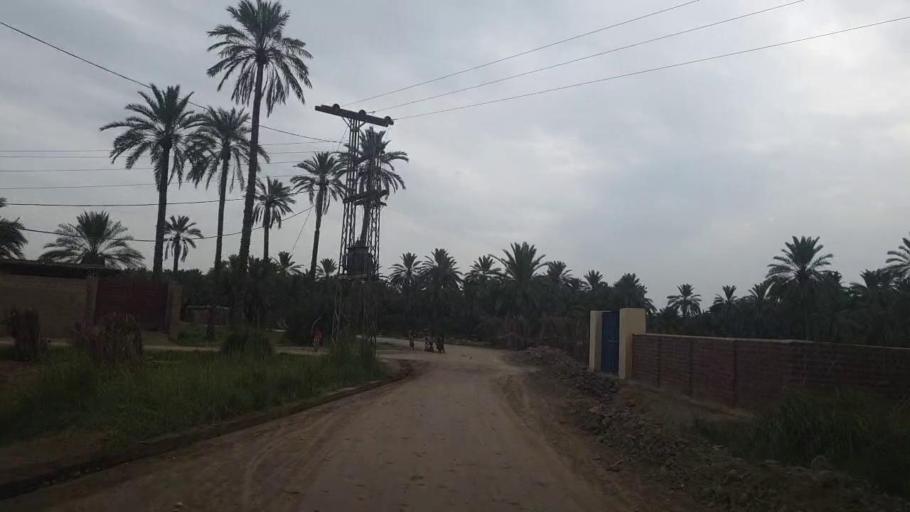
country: PK
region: Sindh
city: Khairpur
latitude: 27.5758
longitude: 68.7453
